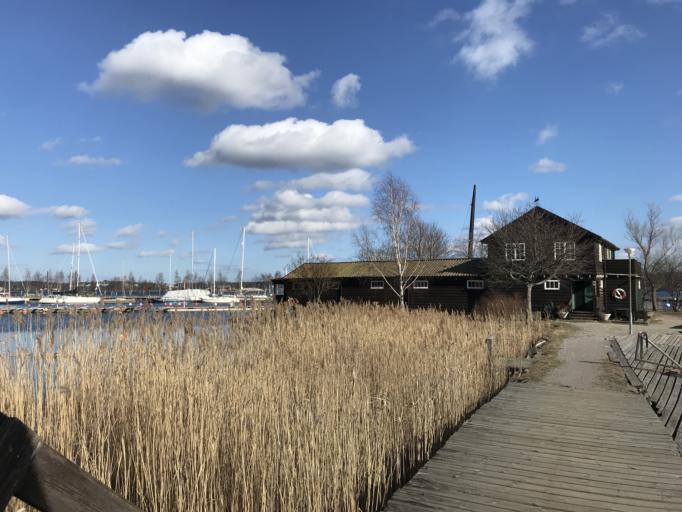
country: SE
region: Stockholm
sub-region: Nacka Kommun
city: Nacka
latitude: 59.3272
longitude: 18.1509
